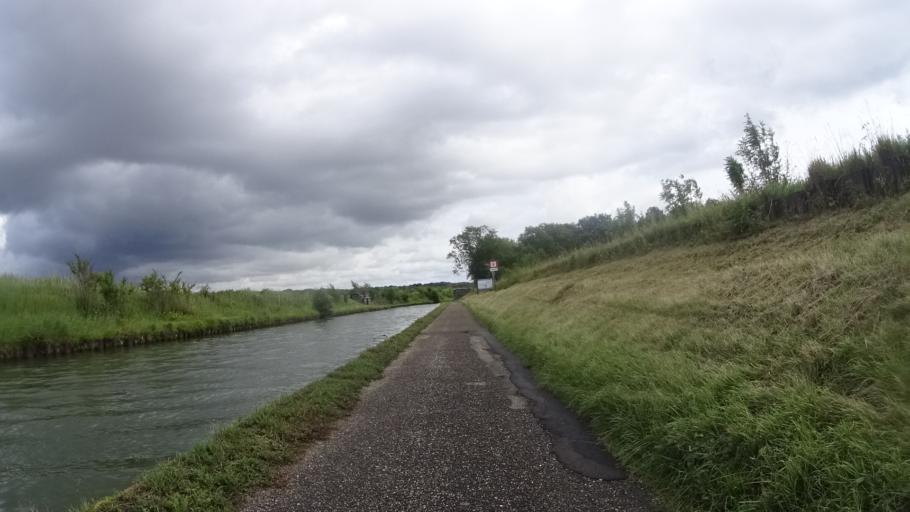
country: FR
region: Lorraine
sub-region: Departement de la Moselle
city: Lorquin
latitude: 48.7042
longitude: 6.9001
